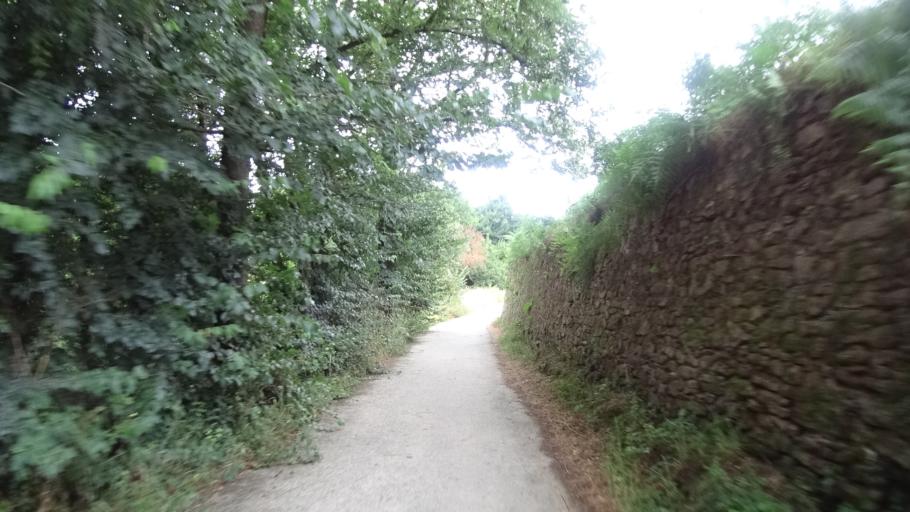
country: FR
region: Pays de la Loire
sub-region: Departement de la Loire-Atlantique
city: Le Pellerin
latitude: 47.2055
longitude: -1.7696
